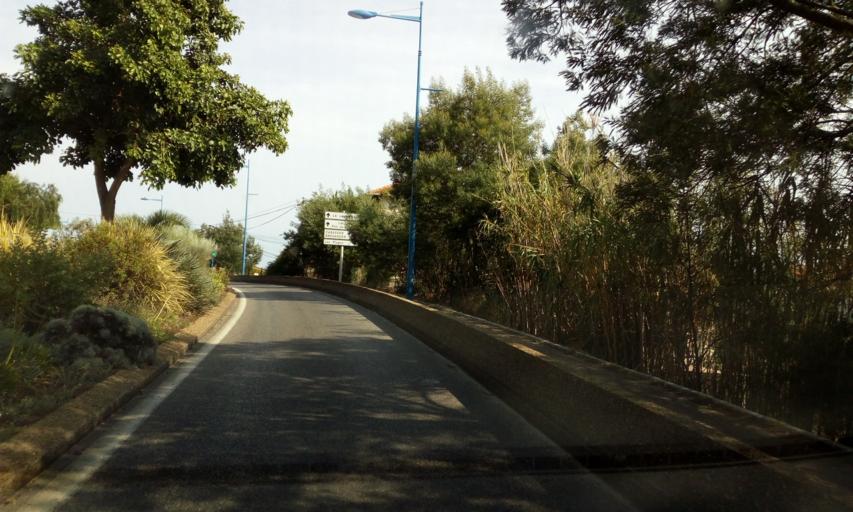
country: FR
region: Provence-Alpes-Cote d'Azur
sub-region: Departement du Var
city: Bormes-les-Mimosas
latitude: 43.1421
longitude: 6.3379
